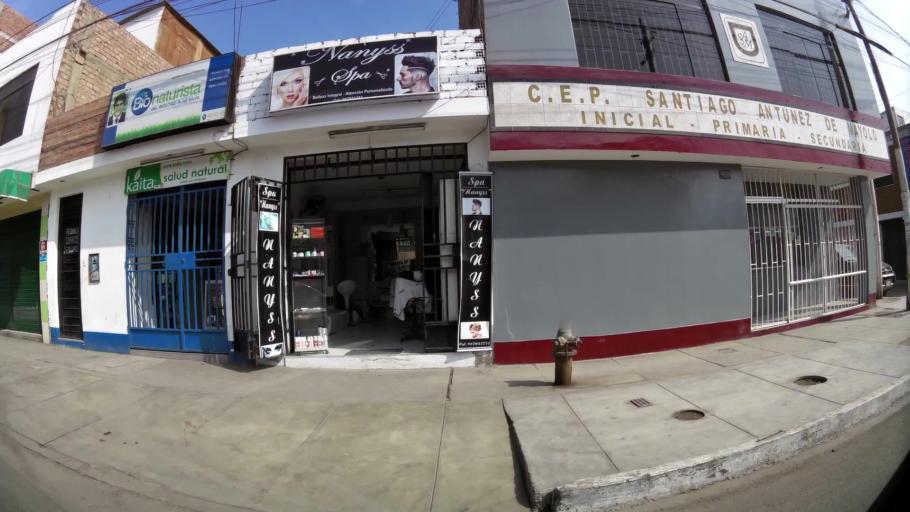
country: PE
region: Lima
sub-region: Lima
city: Santa Rosa
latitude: -11.7765
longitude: -77.1666
